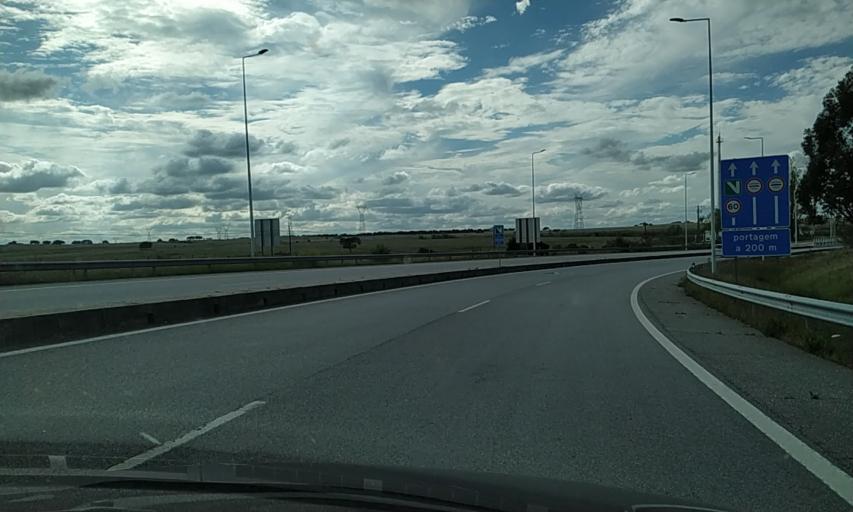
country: PT
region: Evora
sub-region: Evora
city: Evora
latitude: 38.6421
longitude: -7.8538
